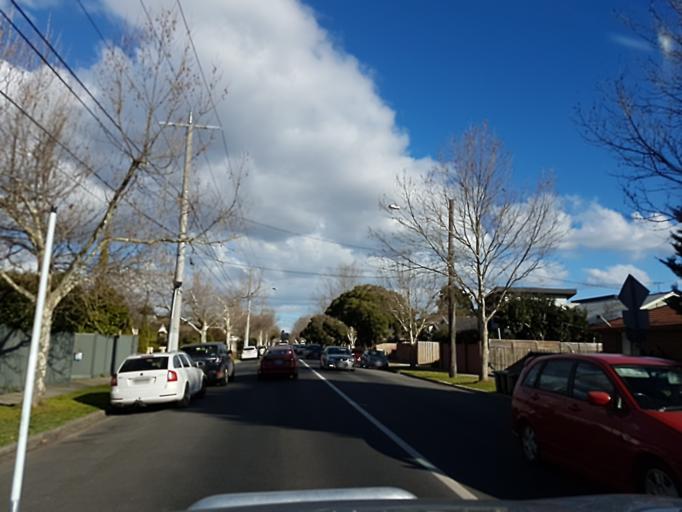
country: AU
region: Victoria
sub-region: Darebin
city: Fairfield
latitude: -37.7761
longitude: 145.0256
